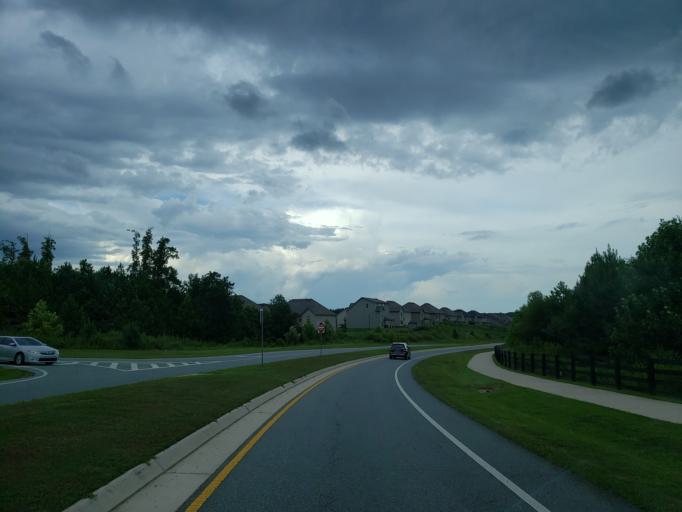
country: US
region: Georgia
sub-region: Bartow County
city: Emerson
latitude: 34.0302
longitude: -84.7735
